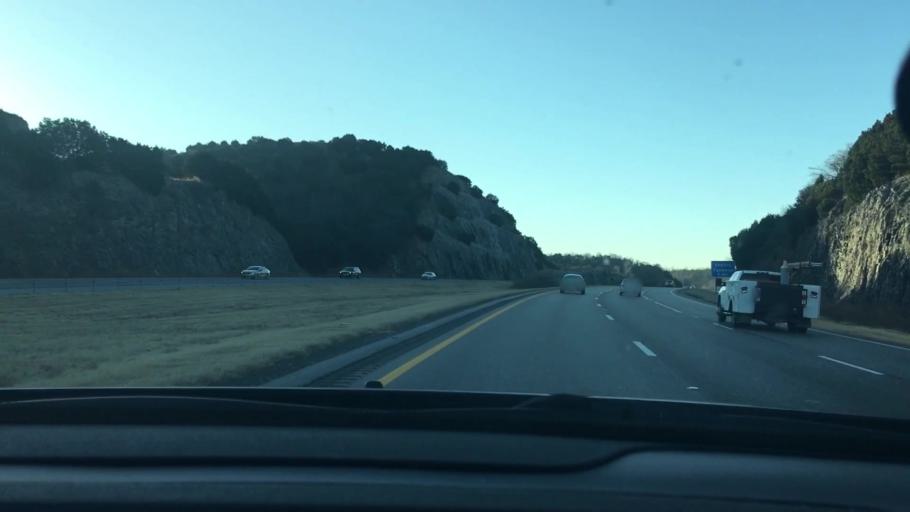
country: US
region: Oklahoma
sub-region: Murray County
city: Davis
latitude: 34.4430
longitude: -97.1291
